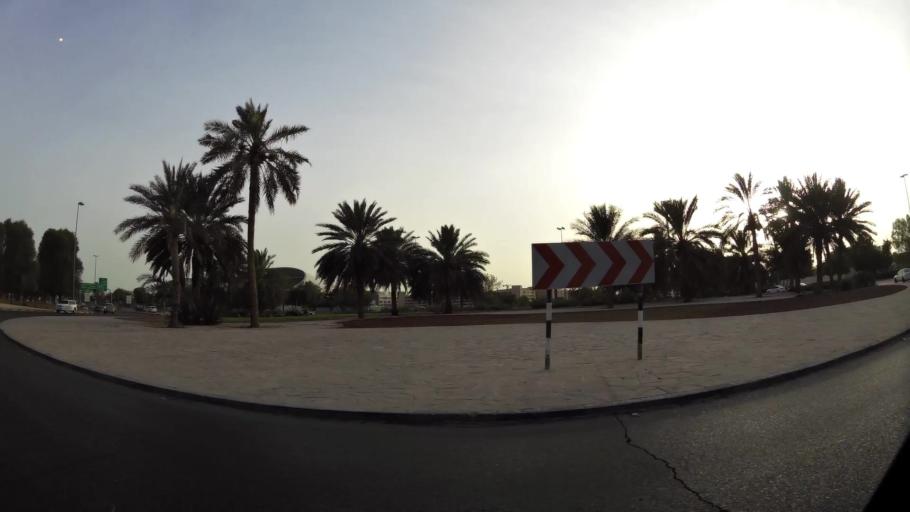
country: AE
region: Abu Dhabi
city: Al Ain
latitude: 24.2483
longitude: 55.7202
